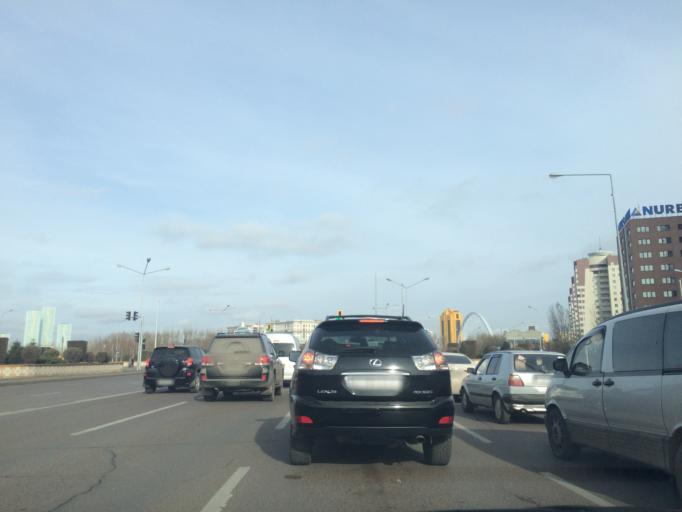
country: KZ
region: Astana Qalasy
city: Astana
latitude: 51.1464
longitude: 71.4221
